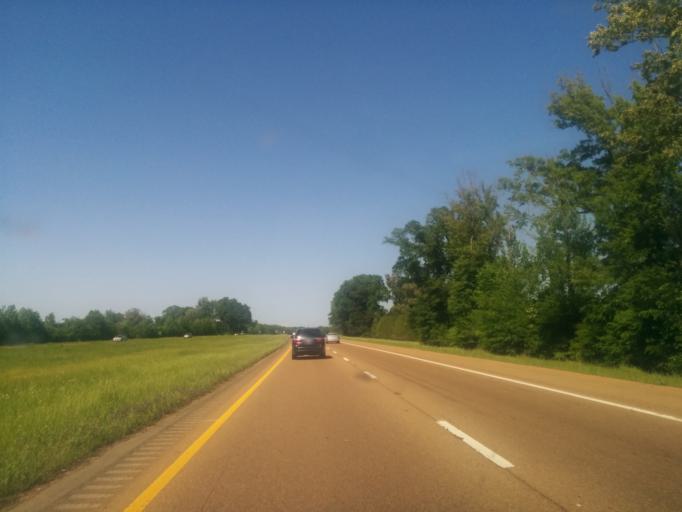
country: US
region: Mississippi
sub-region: Madison County
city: Madison
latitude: 32.4932
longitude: -90.1252
